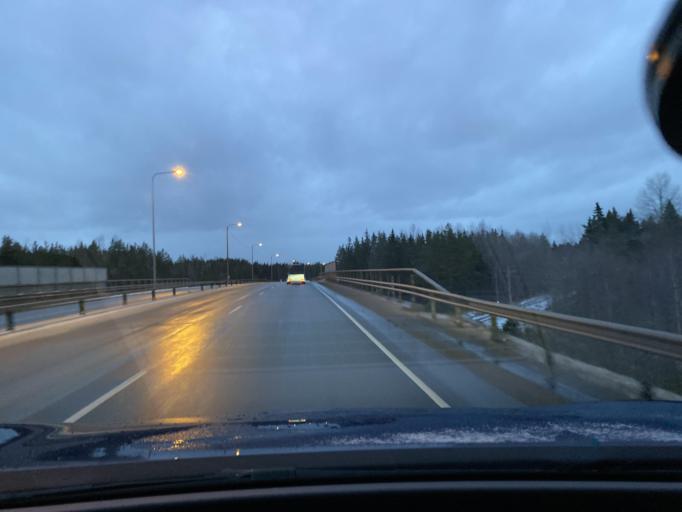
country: FI
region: Satakunta
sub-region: Rauma
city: Rauma
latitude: 61.1426
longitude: 21.5511
